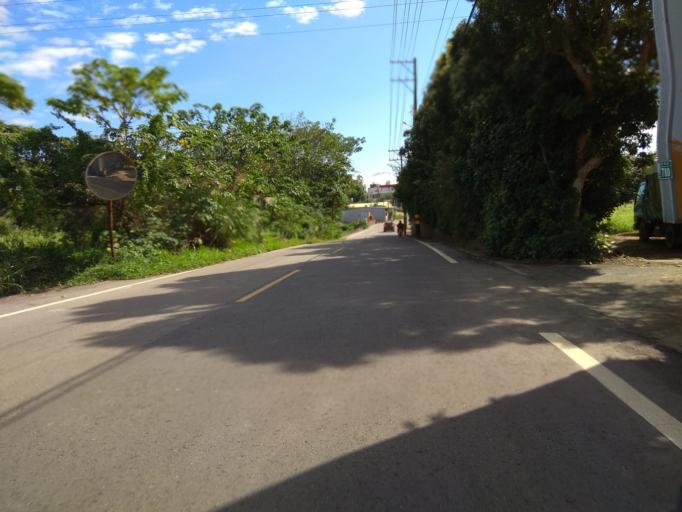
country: TW
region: Taiwan
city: Taoyuan City
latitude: 25.0402
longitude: 121.1262
